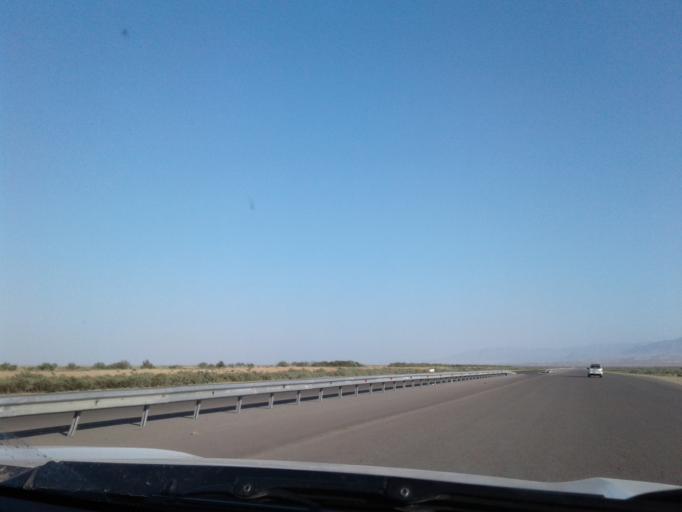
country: TM
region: Balkan
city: Serdar
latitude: 38.8412
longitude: 56.6184
